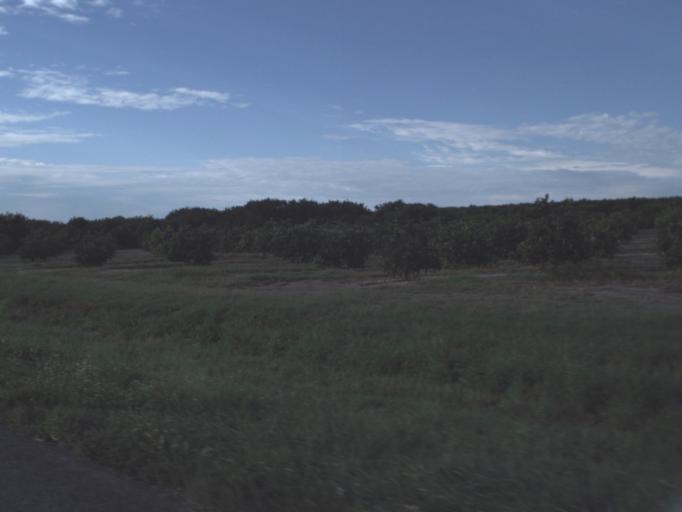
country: US
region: Florida
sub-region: Highlands County
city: Lake Placid
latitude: 27.2456
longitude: -81.3369
